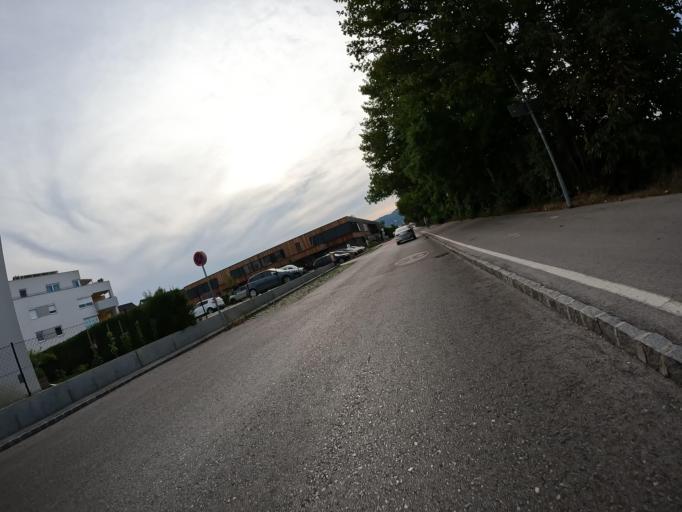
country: AT
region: Lower Austria
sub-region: Politischer Bezirk Baden
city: Traiskirchen
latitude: 48.0192
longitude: 16.3011
